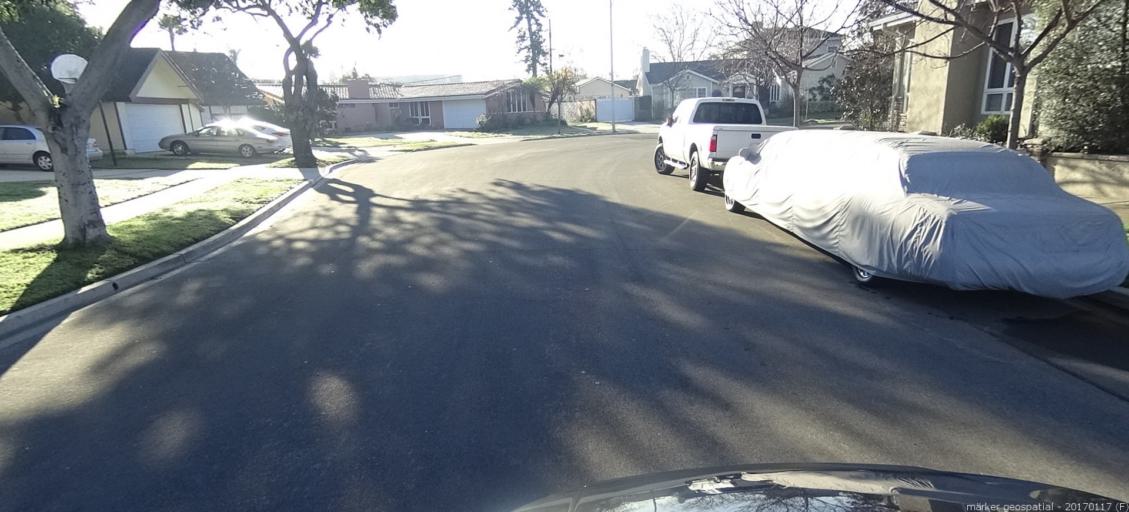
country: US
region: California
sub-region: Orange County
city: Rossmoor
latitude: 33.7785
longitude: -118.0793
